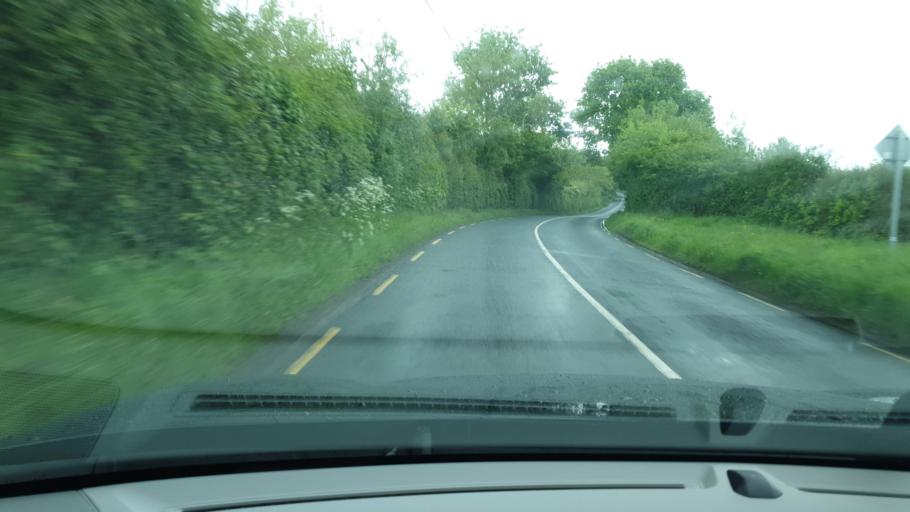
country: IE
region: Leinster
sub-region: Laois
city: Mountrath
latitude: 53.0630
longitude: -7.4135
